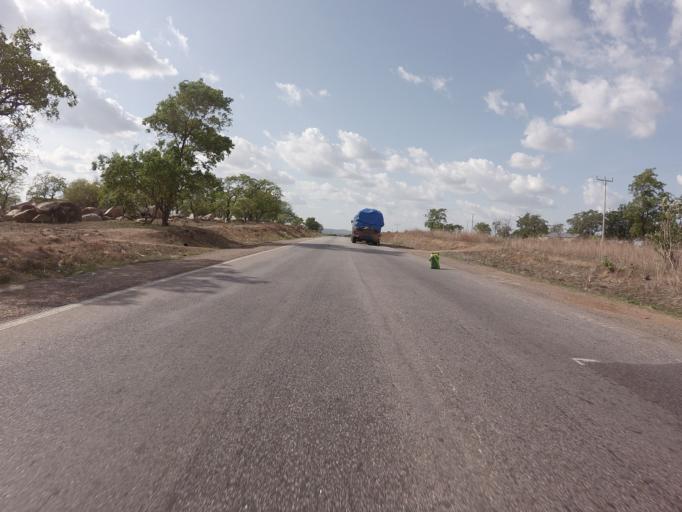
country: GH
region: Upper East
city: Bolgatanga
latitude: 10.5708
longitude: -0.8331
